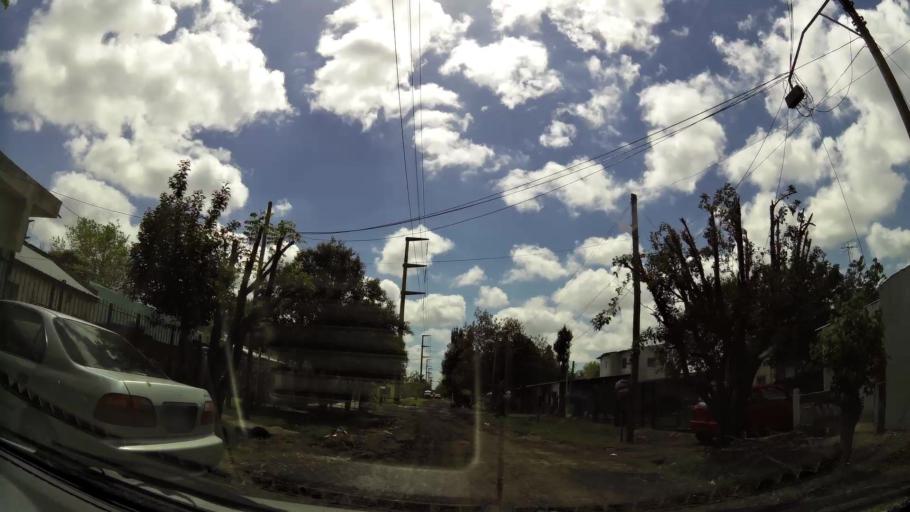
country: AR
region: Buenos Aires
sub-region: Partido de Quilmes
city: Quilmes
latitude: -34.8388
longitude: -58.2344
